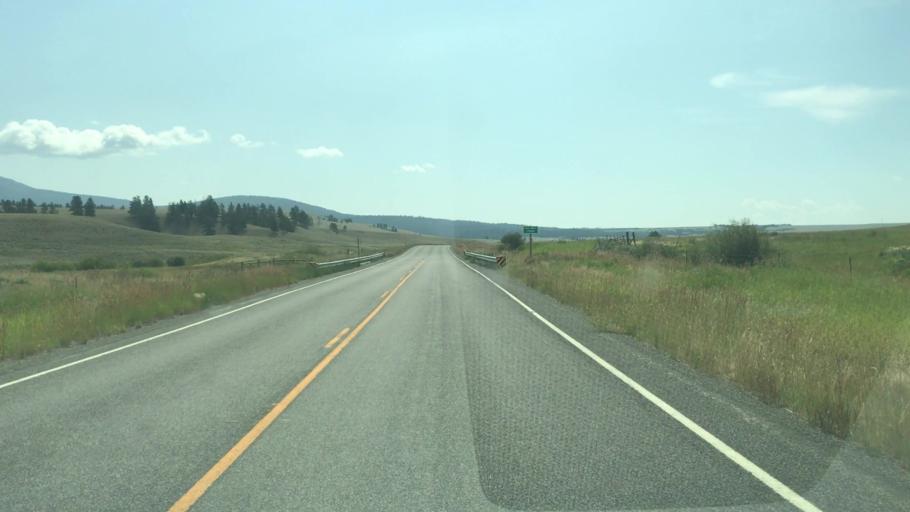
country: US
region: Montana
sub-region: Lewis and Clark County
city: Lincoln
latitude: 46.7442
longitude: -112.6882
